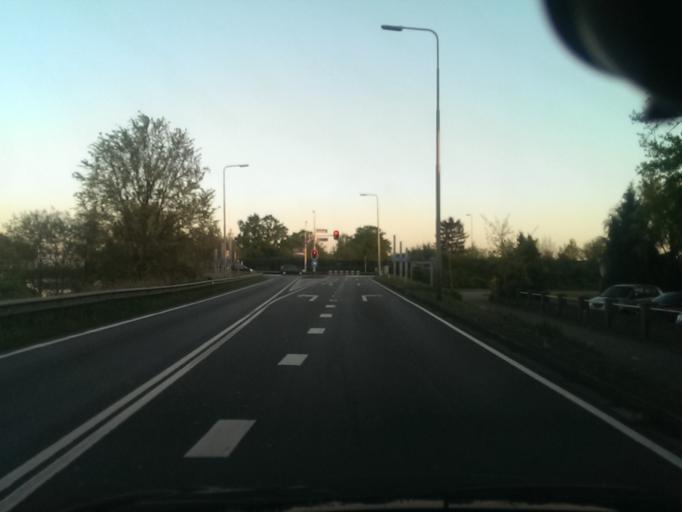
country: NL
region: Limburg
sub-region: Gemeente Nederweert
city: Nederweert
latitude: 51.2812
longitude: 5.7546
